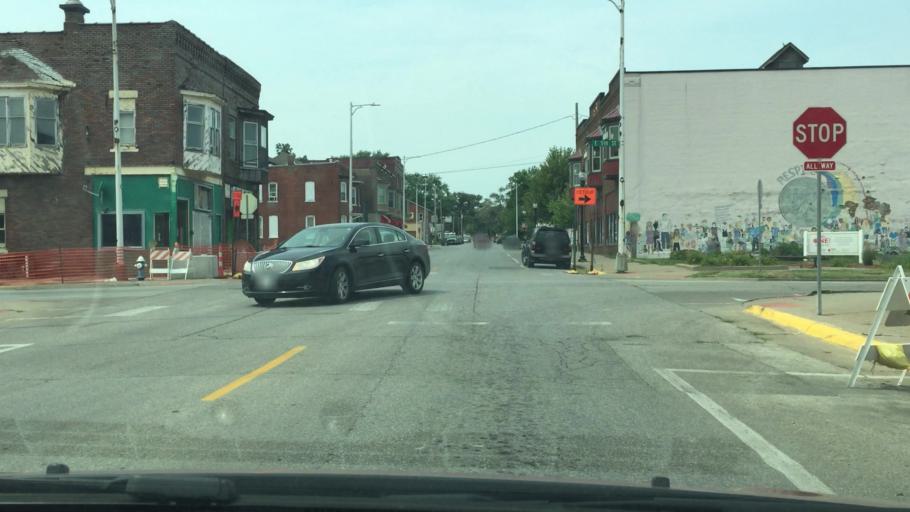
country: US
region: Iowa
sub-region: Muscatine County
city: Muscatine
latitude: 41.4259
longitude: -91.0437
